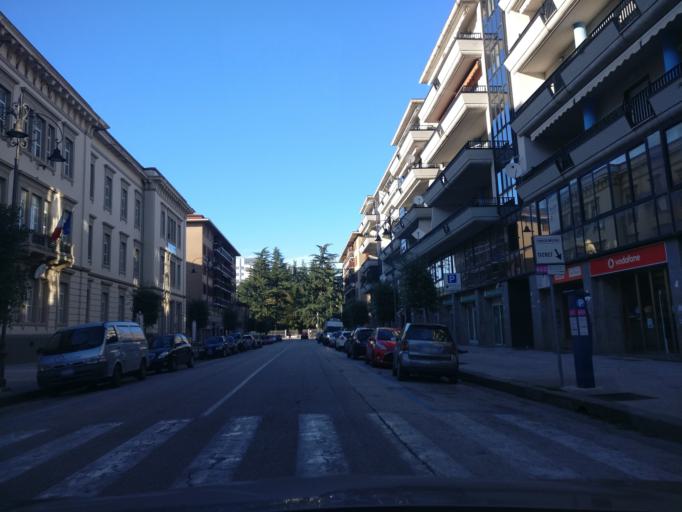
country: IT
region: Campania
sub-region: Provincia di Avellino
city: Avellino
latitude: 40.9138
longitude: 14.7832
